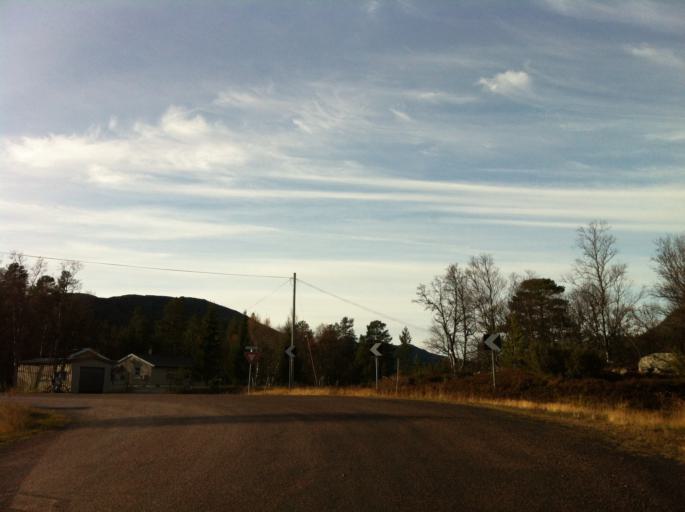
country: NO
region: Hedmark
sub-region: Engerdal
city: Engerdal
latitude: 62.0843
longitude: 12.0821
